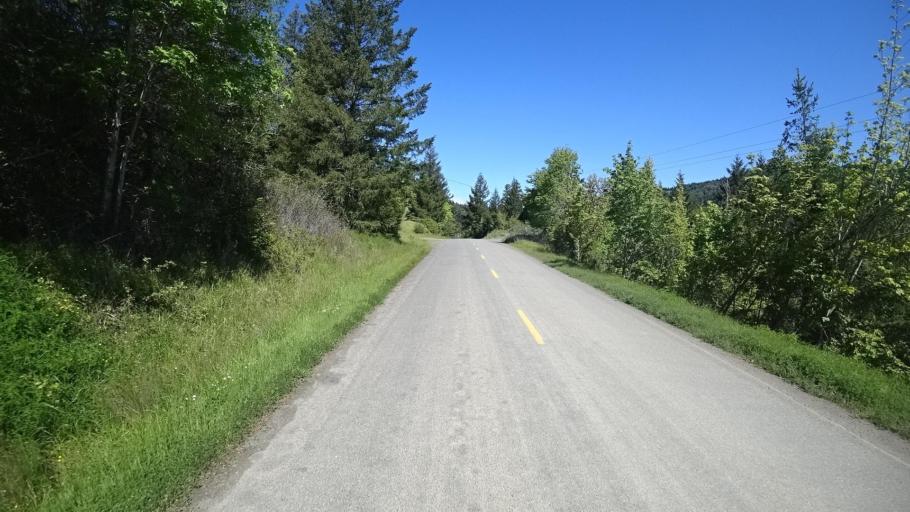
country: US
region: California
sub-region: Humboldt County
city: Rio Dell
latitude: 40.2560
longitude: -124.1911
